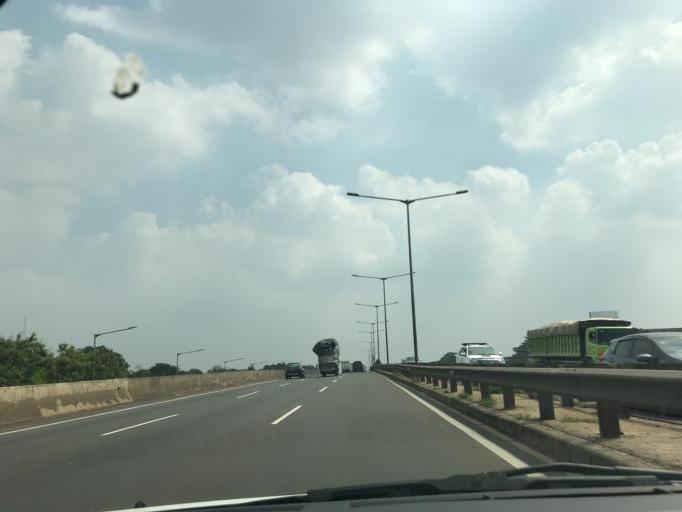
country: ID
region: West Java
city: Ciputat
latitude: -6.2199
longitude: 106.7463
